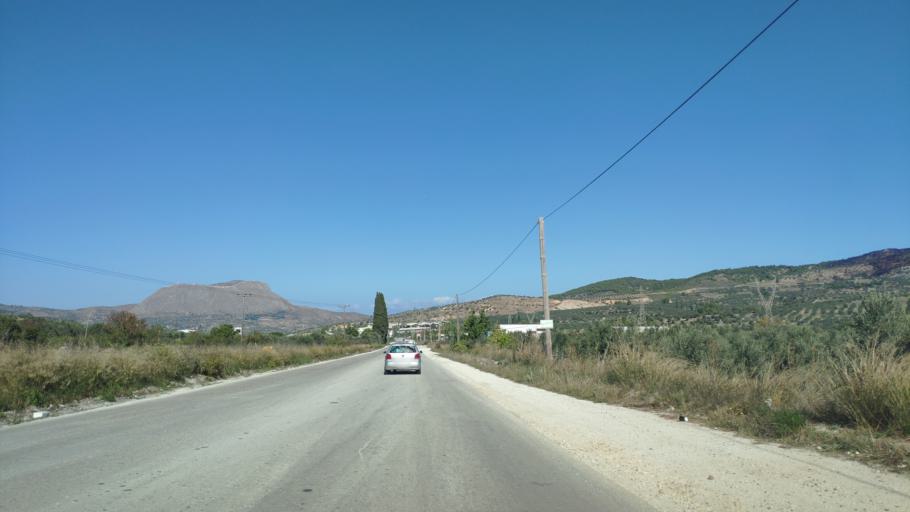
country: GR
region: Peloponnese
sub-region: Nomos Korinthias
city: Athikia
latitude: 37.8412
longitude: 22.8994
